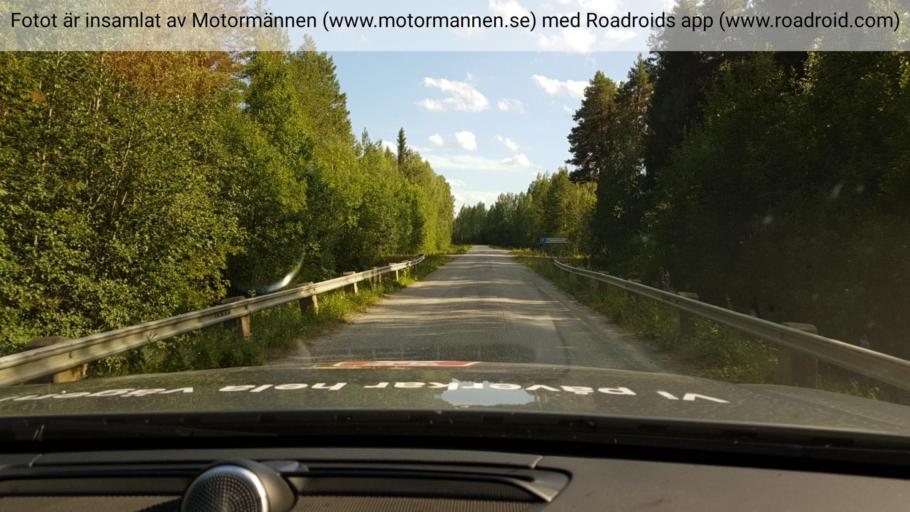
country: SE
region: Vaesterbotten
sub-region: Dorotea Kommun
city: Dorotea
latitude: 63.9160
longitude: 16.2659
